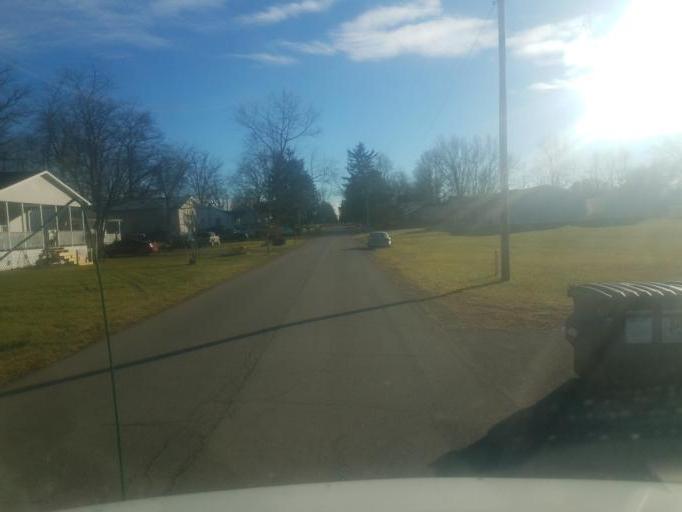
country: US
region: Ohio
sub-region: Richland County
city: Mansfield
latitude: 40.7811
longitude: -82.5483
